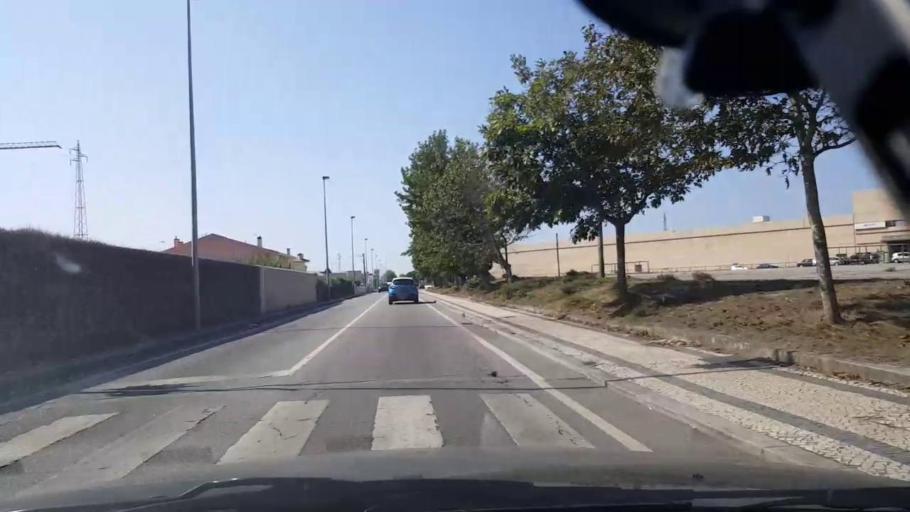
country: PT
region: Porto
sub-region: Vila do Conde
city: Vila do Conde
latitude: 41.3789
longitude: -8.7360
